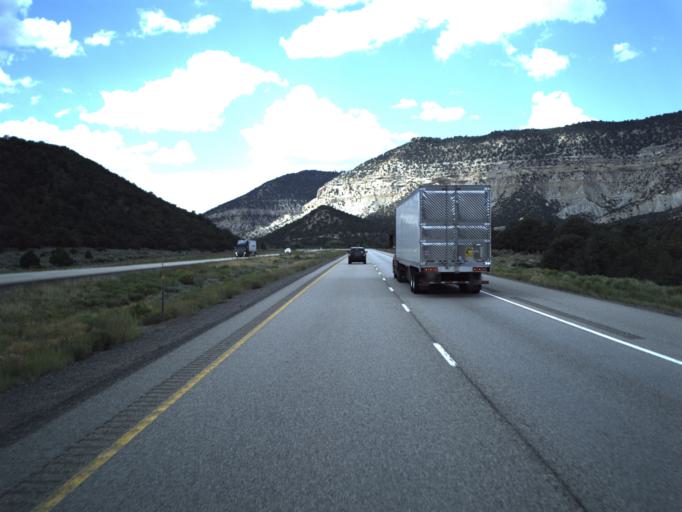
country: US
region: Utah
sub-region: Wayne County
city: Loa
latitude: 38.7563
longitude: -111.3997
